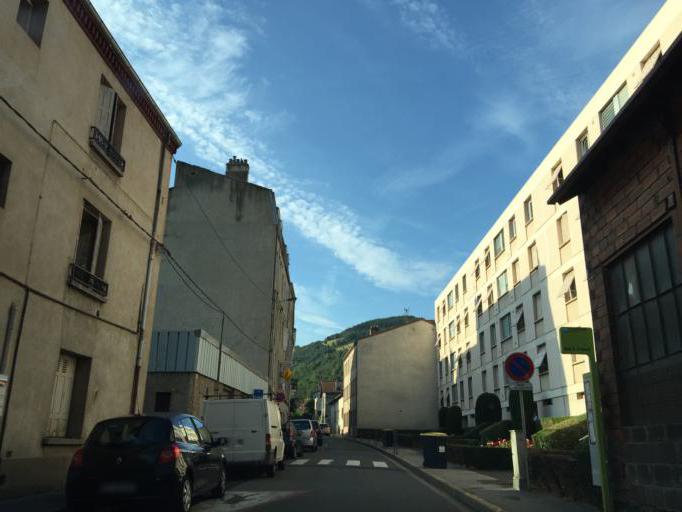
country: FR
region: Rhone-Alpes
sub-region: Departement de la Loire
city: Saint-Jean-Bonnefonds
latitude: 45.4303
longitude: 4.4335
